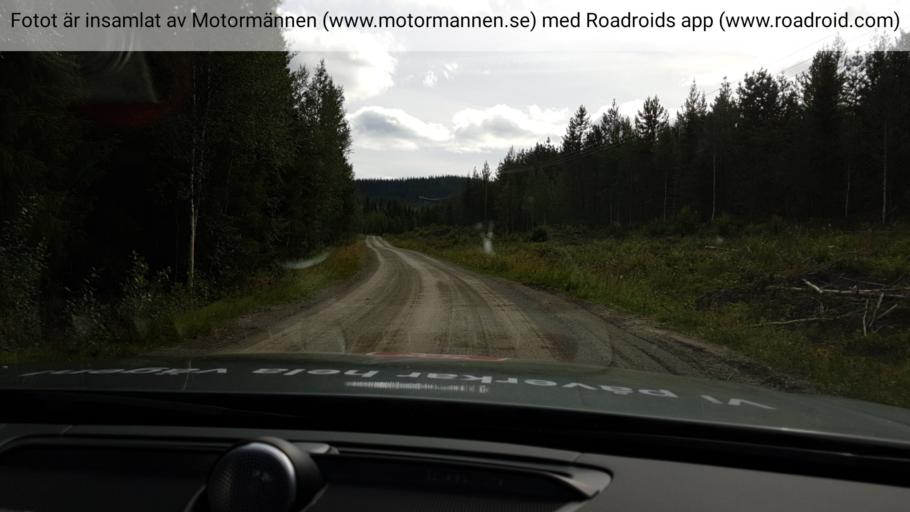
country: SE
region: Jaemtland
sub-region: Stroemsunds Kommun
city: Stroemsund
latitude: 64.5314
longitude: 15.2639
